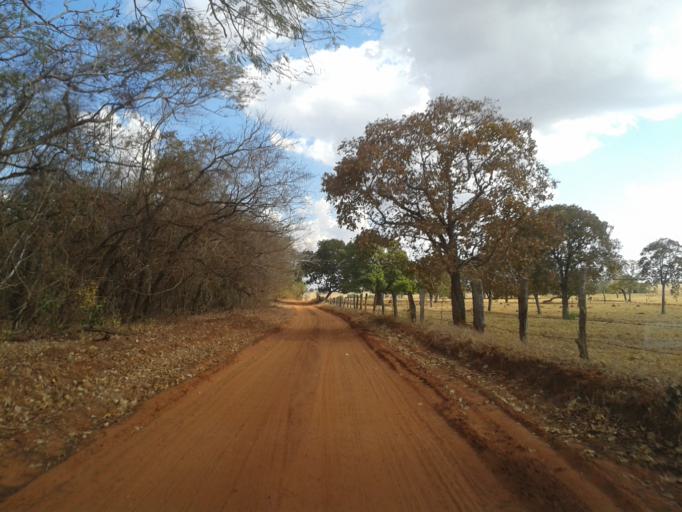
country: BR
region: Minas Gerais
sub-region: Santa Vitoria
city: Santa Vitoria
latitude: -19.2631
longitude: -49.9866
